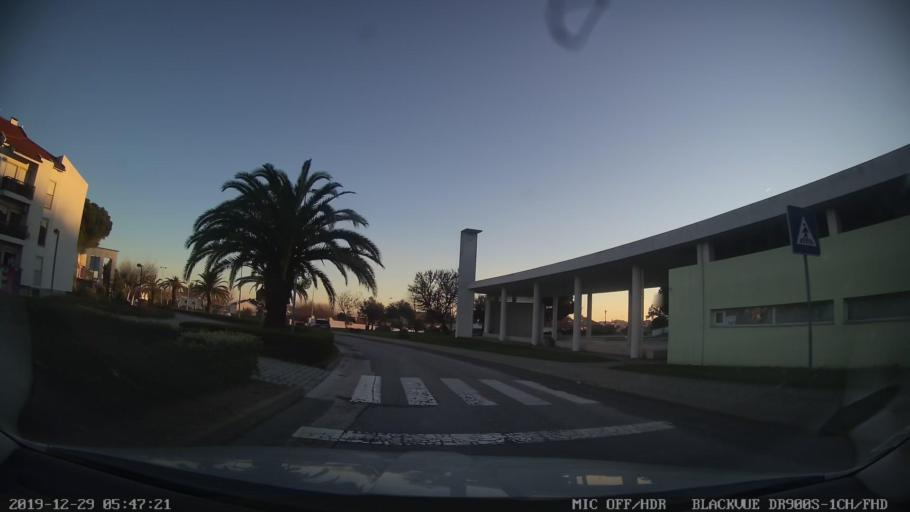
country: PT
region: Castelo Branco
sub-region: Idanha-A-Nova
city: Idanha-a-Nova
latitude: 39.9249
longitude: -7.2438
